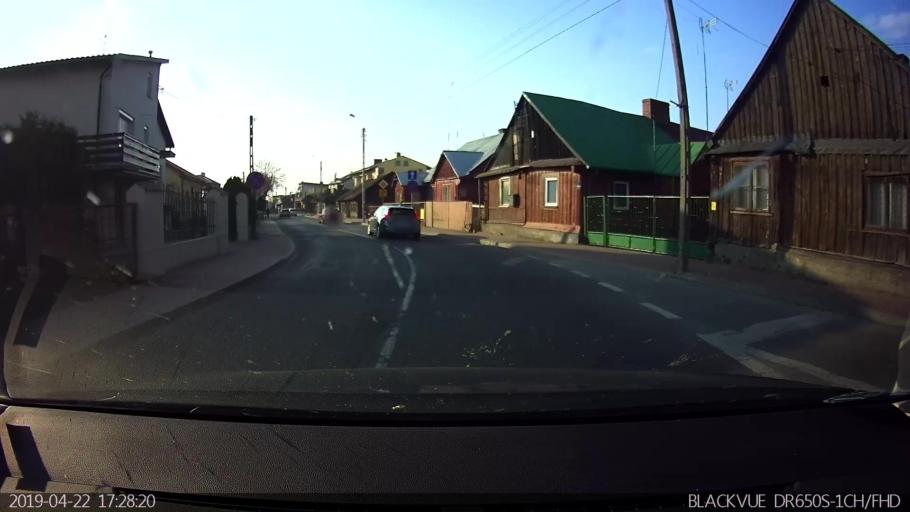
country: PL
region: Masovian Voivodeship
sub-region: Powiat sokolowski
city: Sokolow Podlaski
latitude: 52.4023
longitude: 22.2602
